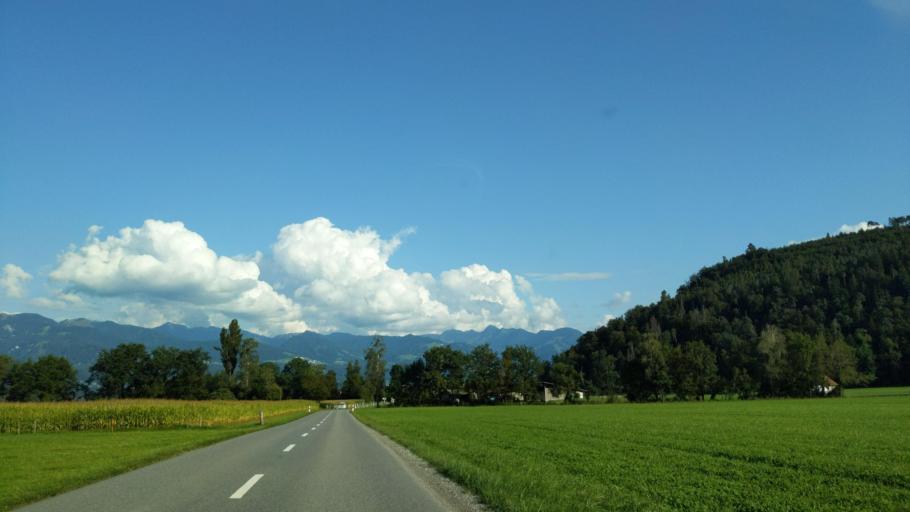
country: CH
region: Saint Gallen
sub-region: Wahlkreis Rheintal
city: Eichberg
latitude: 47.3342
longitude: 9.5463
